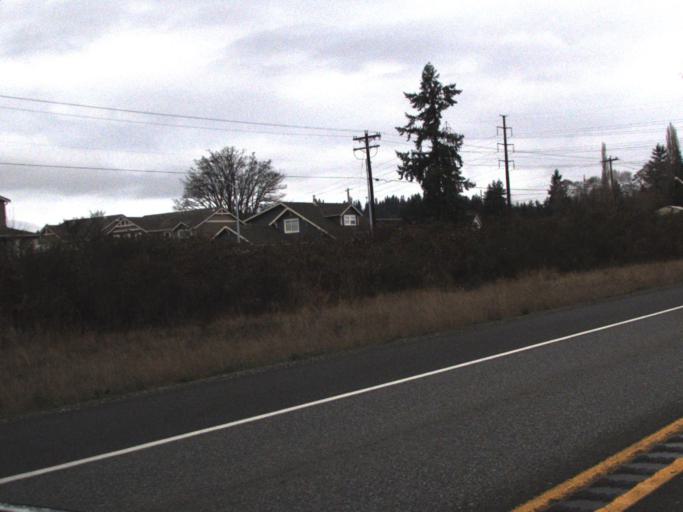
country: US
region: Washington
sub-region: Snohomish County
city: Snohomish
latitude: 47.9201
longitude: -122.1083
